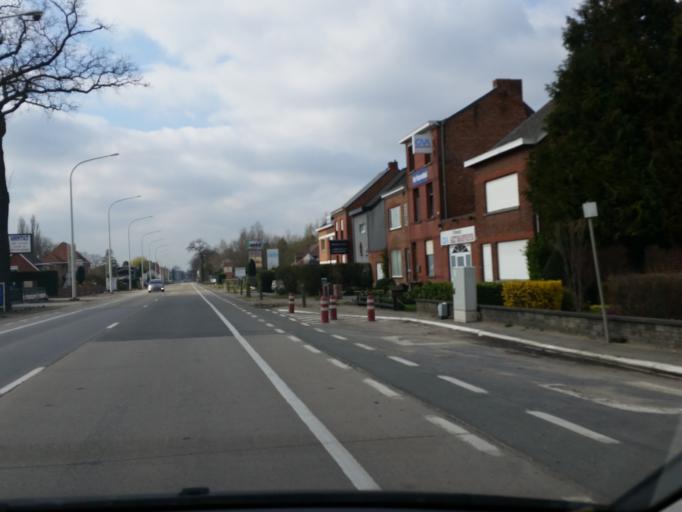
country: BE
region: Flanders
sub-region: Provincie Antwerpen
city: Bonheiden
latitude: 50.9912
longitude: 4.5375
